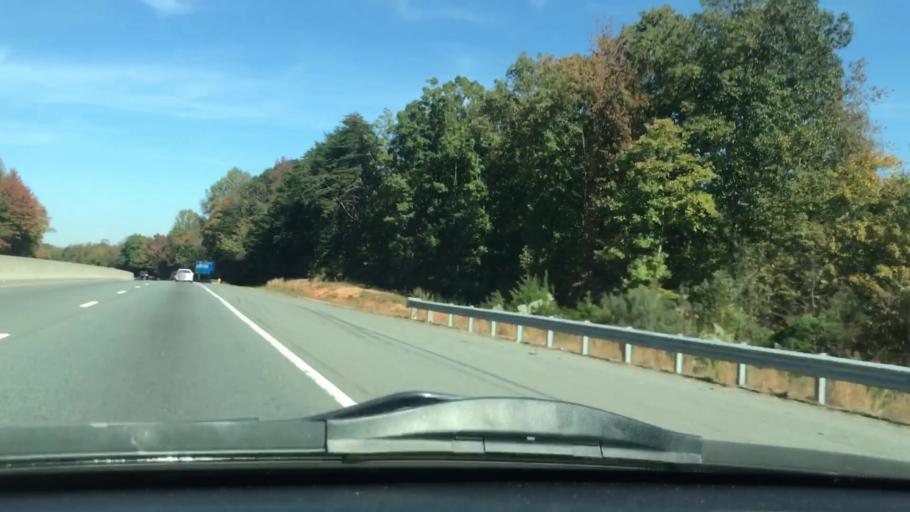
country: US
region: North Carolina
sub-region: Randolph County
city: Asheboro
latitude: 35.7244
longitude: -79.8248
